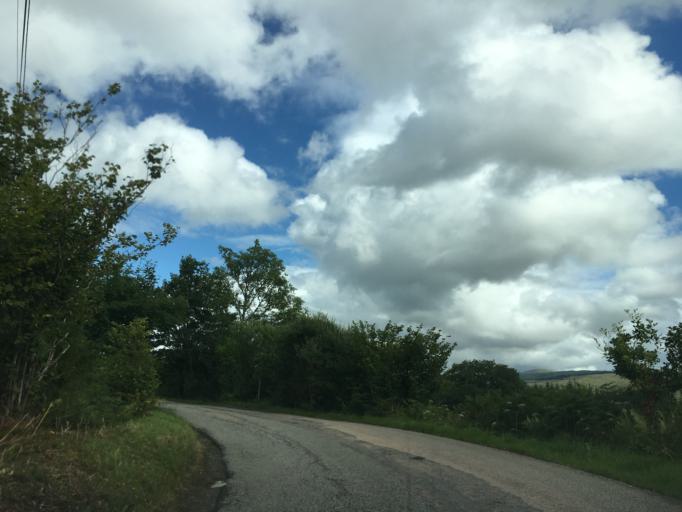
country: GB
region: Scotland
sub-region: Argyll and Bute
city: Oban
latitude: 56.2781
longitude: -5.2761
